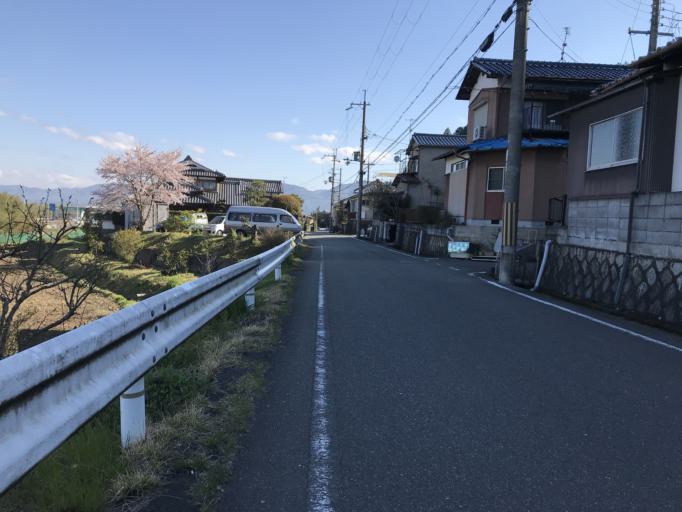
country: JP
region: Kyoto
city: Kameoka
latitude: 35.0046
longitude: 135.5585
